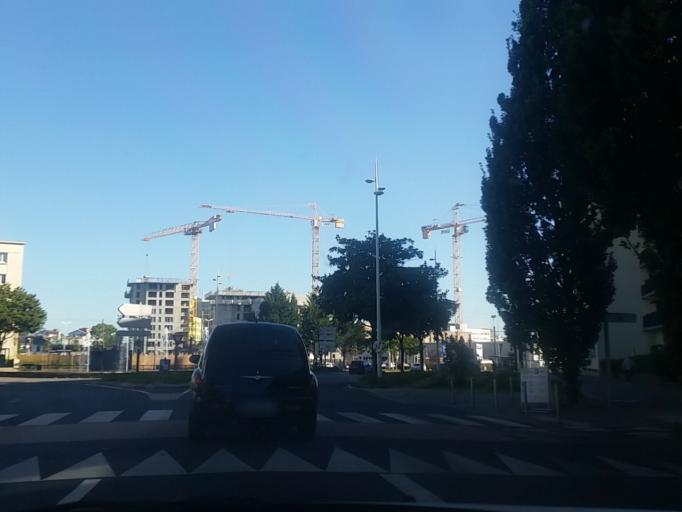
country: FR
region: Pays de la Loire
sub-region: Departement de la Loire-Atlantique
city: Reze
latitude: 47.1910
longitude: -1.5478
